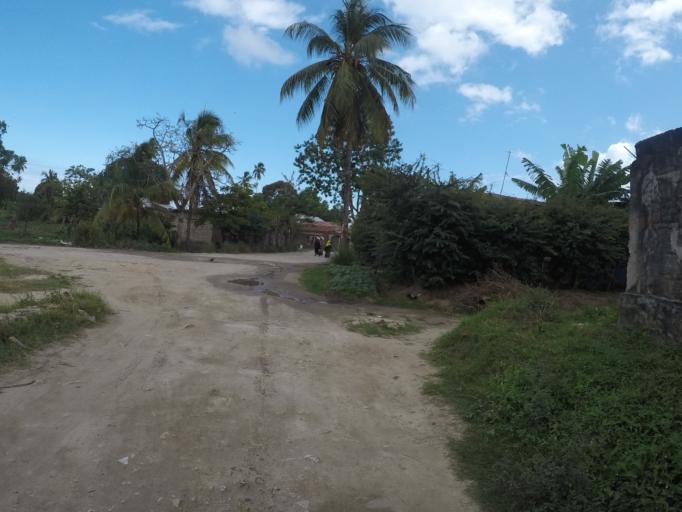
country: TZ
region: Zanzibar Urban/West
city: Zanzibar
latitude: -6.1860
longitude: 39.2132
